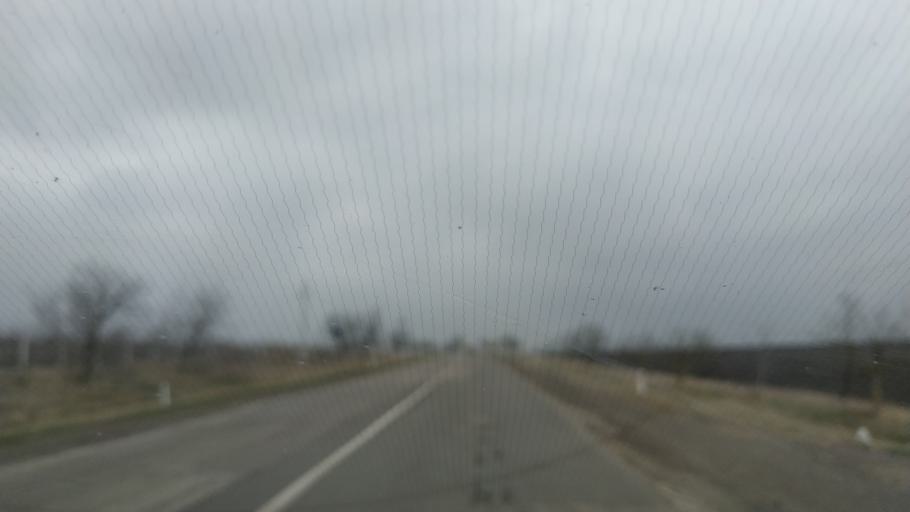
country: MD
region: Gagauzia
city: Comrat
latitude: 46.2689
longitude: 28.7325
